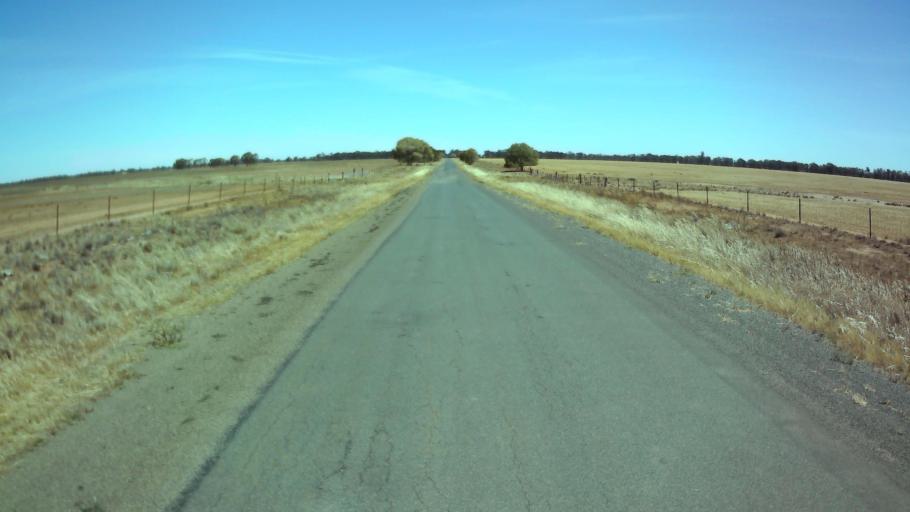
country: AU
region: New South Wales
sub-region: Weddin
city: Grenfell
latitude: -33.8516
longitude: 147.6955
